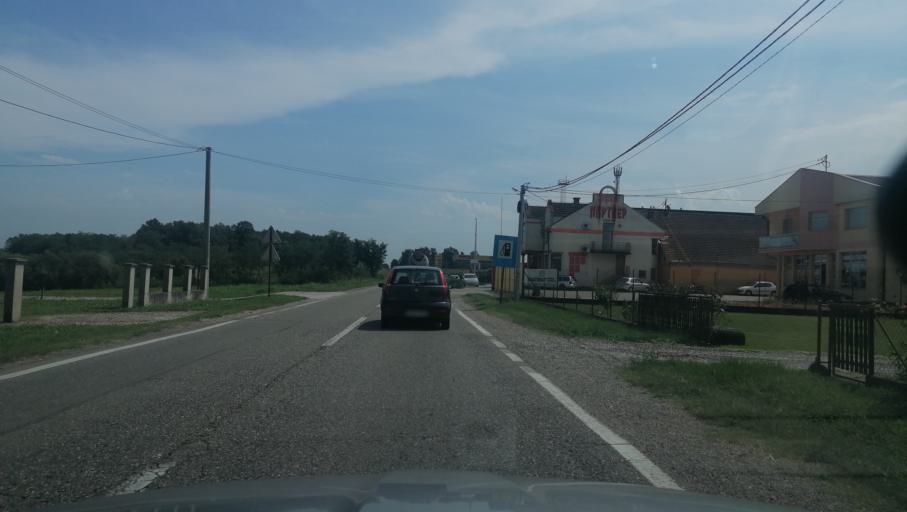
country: BA
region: Republika Srpska
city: Velika Obarska
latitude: 44.8088
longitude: 19.0679
